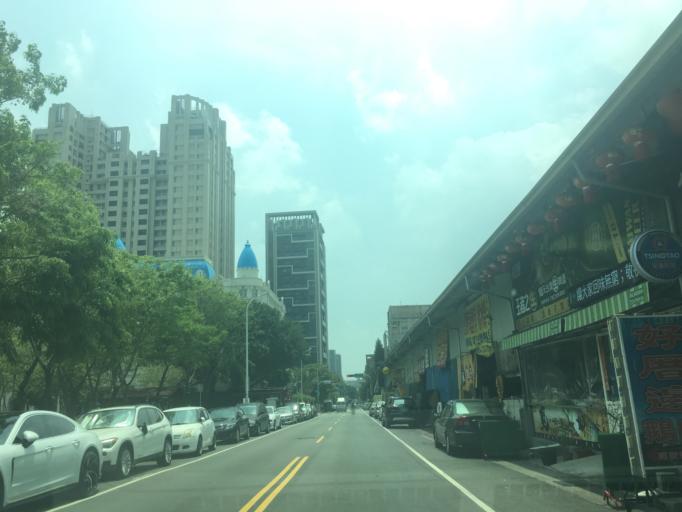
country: TW
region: Taiwan
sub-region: Taichung City
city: Taichung
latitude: 24.1802
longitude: 120.6839
